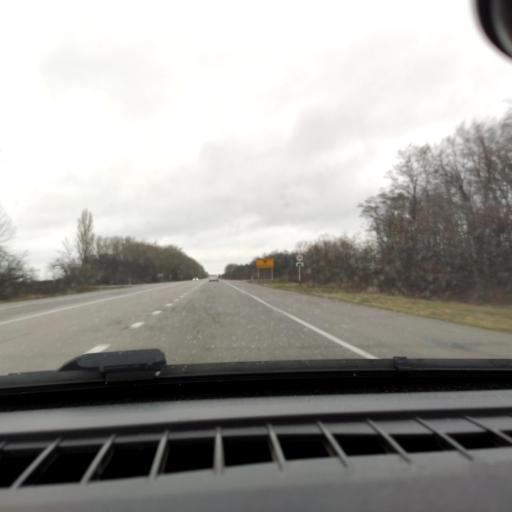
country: RU
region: Voronezj
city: Kolodeznyy
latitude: 51.2674
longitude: 39.0500
